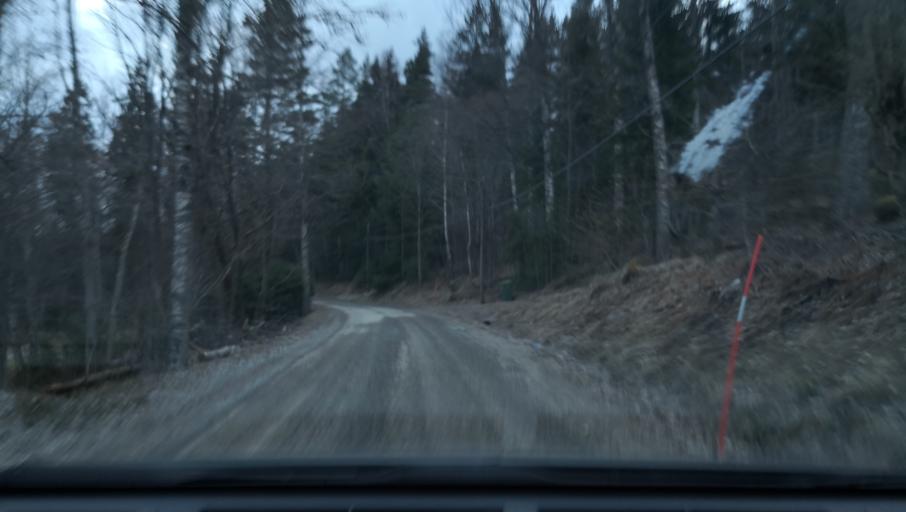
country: SE
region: Vaestmanland
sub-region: Kopings Kommun
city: Kolsva
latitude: 59.5960
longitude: 15.7170
